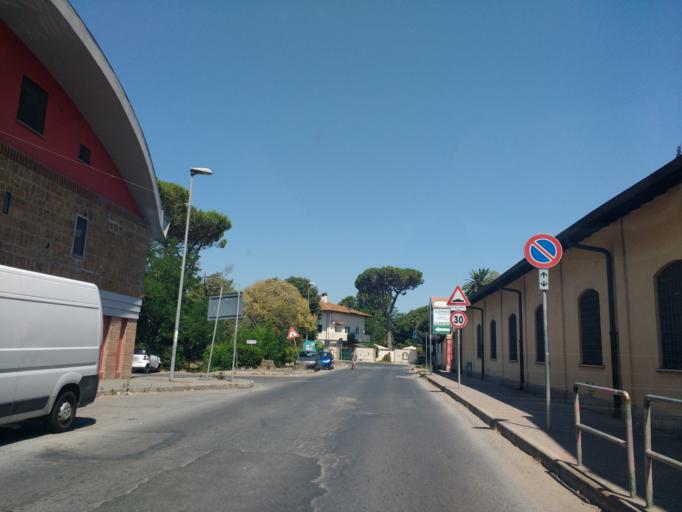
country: IT
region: Latium
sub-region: Citta metropolitana di Roma Capitale
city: Maccarese
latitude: 41.8771
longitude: 12.2149
